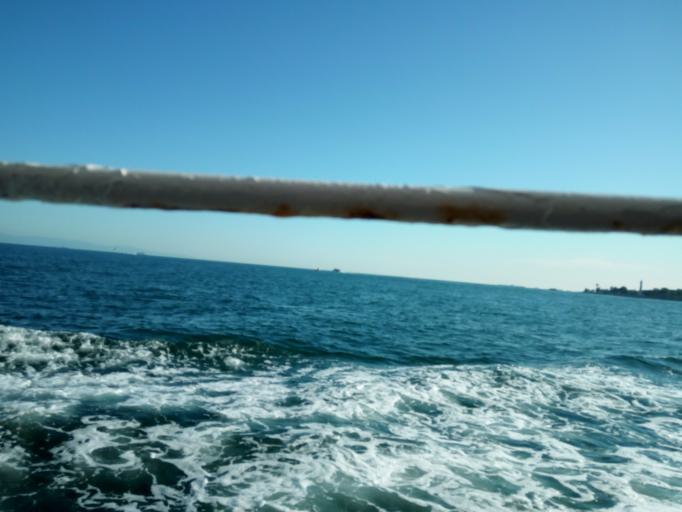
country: TR
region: Istanbul
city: Eminoenue
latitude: 41.0127
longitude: 28.9987
